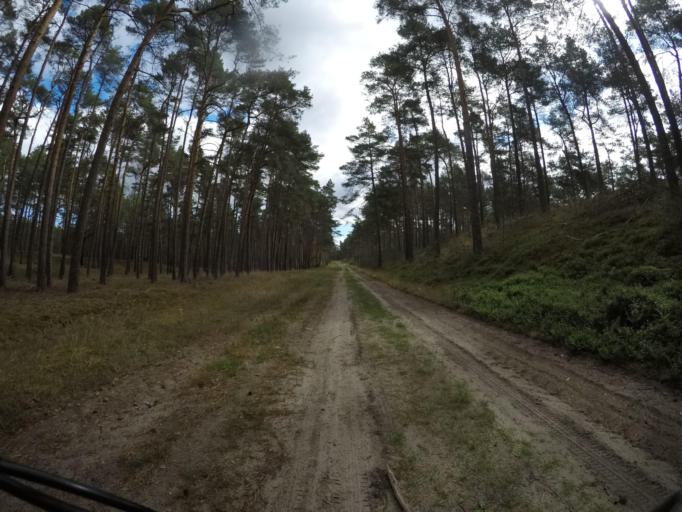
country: DE
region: Lower Saxony
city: Hitzacker
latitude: 53.2378
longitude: 10.9893
